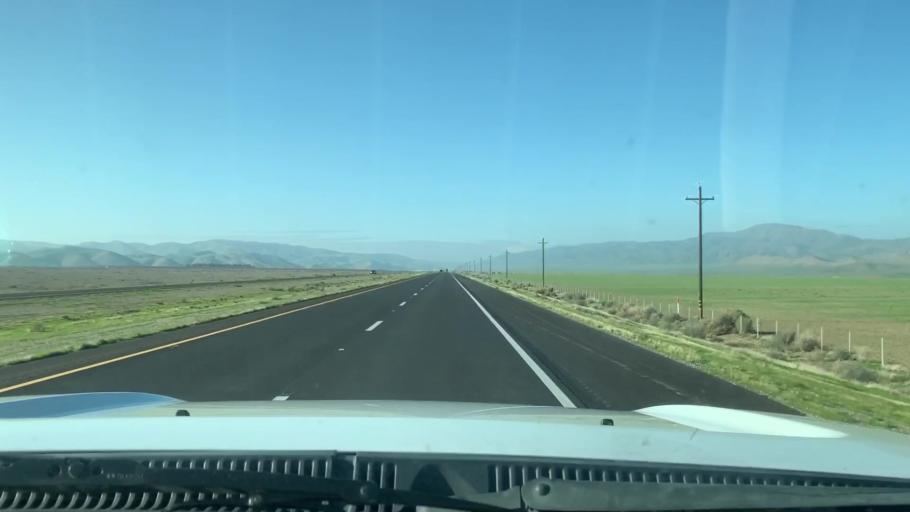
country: US
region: California
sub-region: San Luis Obispo County
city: Shandon
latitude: 35.6598
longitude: -120.0574
